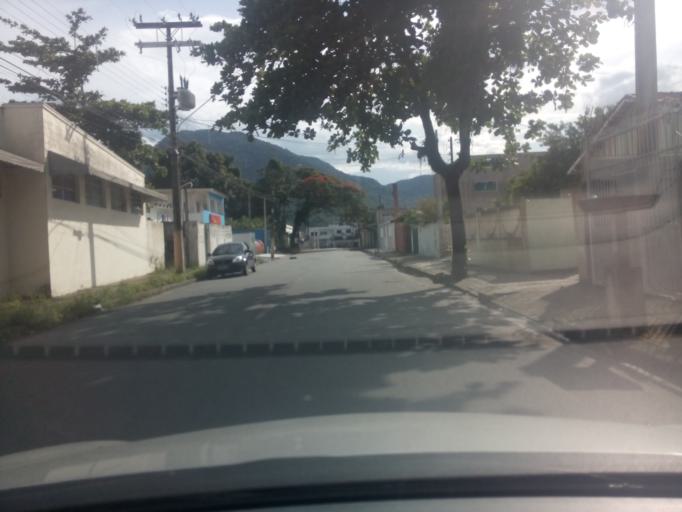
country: BR
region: Sao Paulo
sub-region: Peruibe
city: Peruibe
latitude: -24.3206
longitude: -47.0013
